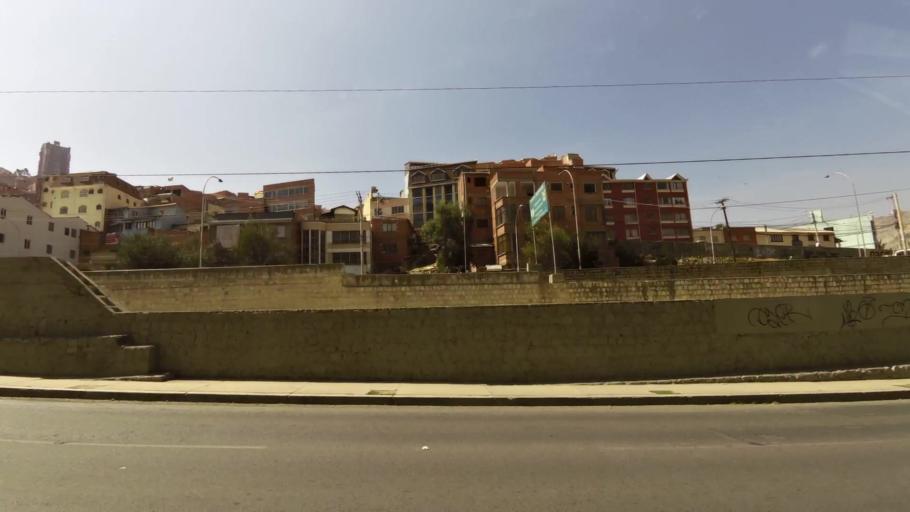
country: BO
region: La Paz
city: La Paz
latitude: -16.5410
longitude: -68.0943
